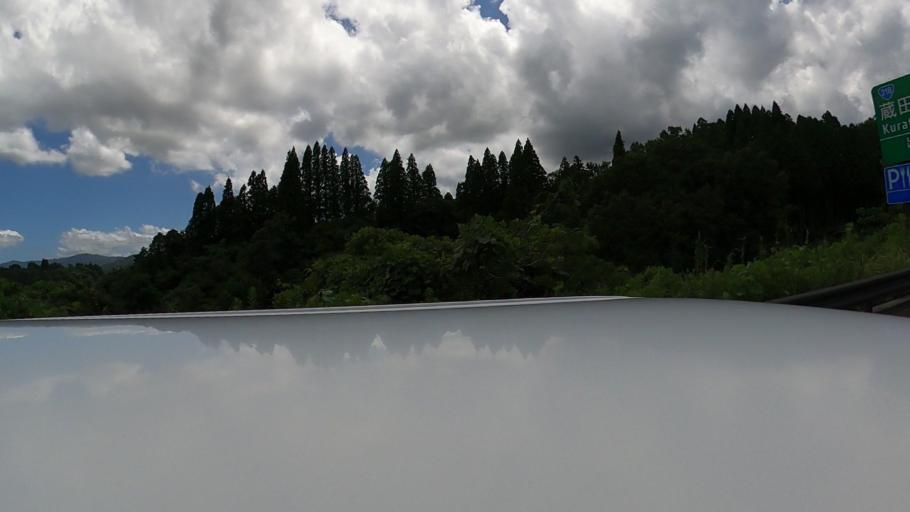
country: JP
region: Miyazaki
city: Nobeoka
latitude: 32.5873
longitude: 131.5100
